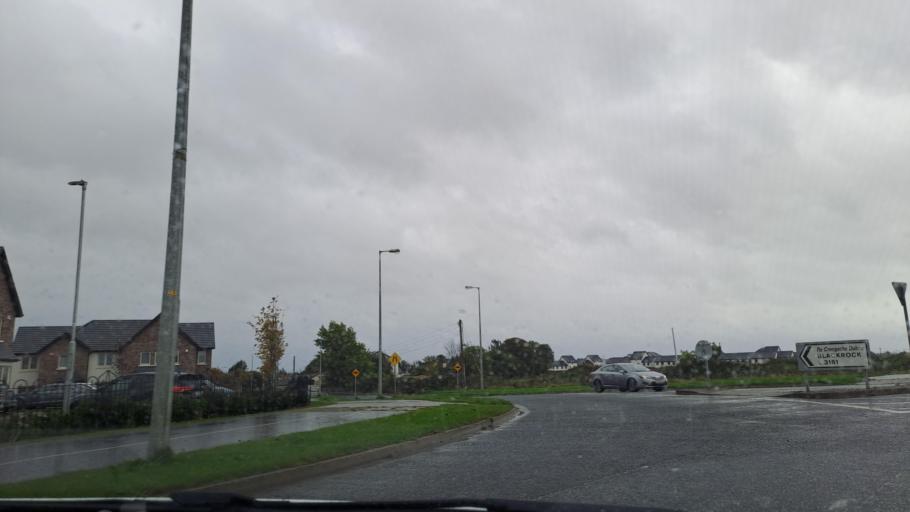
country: IE
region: Leinster
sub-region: Lu
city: Blackrock
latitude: 53.9661
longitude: -6.3973
